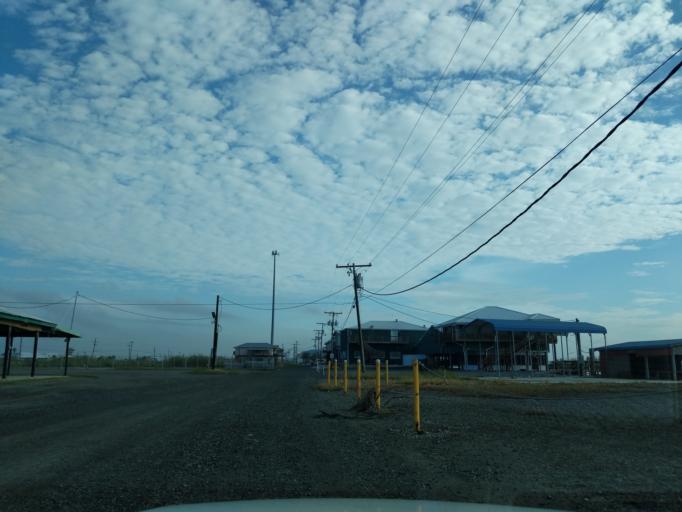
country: US
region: Louisiana
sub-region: Terrebonne Parish
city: Dulac
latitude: 29.2463
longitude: -90.6615
